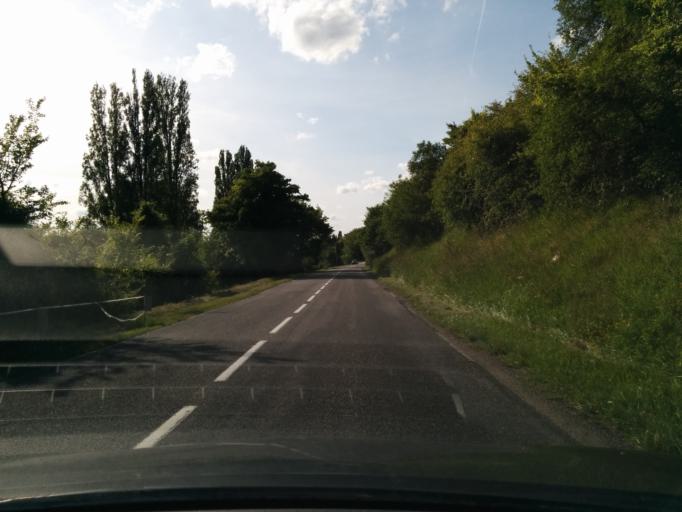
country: FR
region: Haute-Normandie
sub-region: Departement de l'Eure
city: Vernon
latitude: 49.1061
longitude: 1.4785
